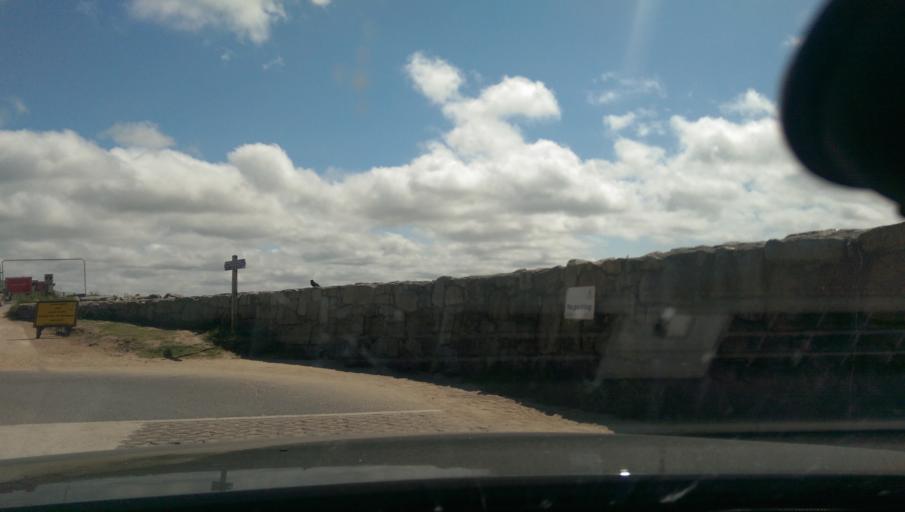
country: GB
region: England
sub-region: Cornwall
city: Marazion
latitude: 50.1281
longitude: -5.5025
